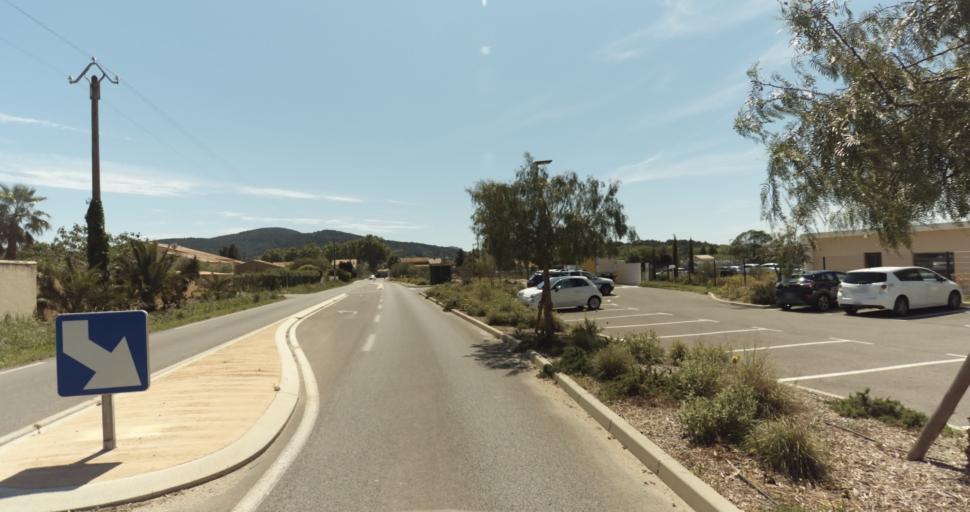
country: FR
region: Provence-Alpes-Cote d'Azur
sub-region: Departement du Var
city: La Crau
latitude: 43.1315
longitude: 6.0774
